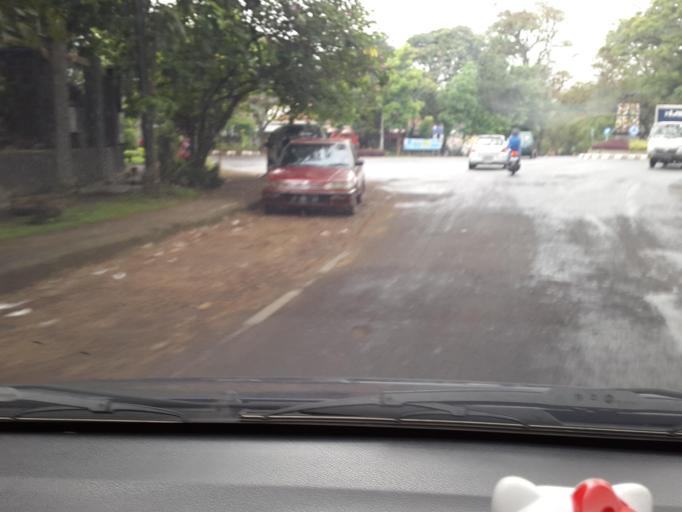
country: ID
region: West Java
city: Bandung
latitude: -6.9044
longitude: 107.6218
